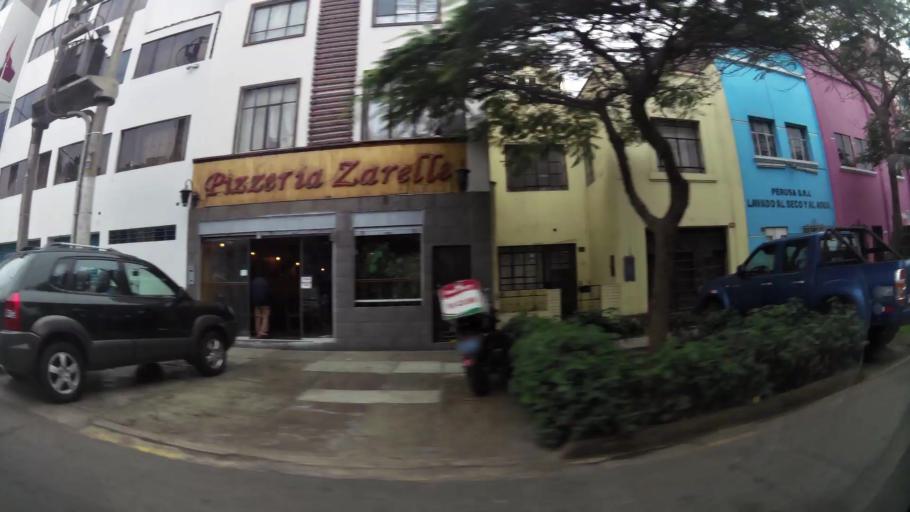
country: PE
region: Lima
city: Lima
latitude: -12.0760
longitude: -77.0515
